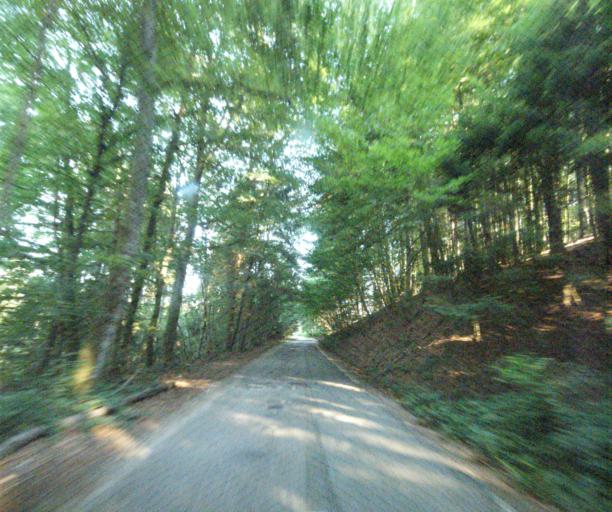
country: FR
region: Lorraine
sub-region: Departement des Vosges
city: Urimenil
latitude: 48.1251
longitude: 6.4280
